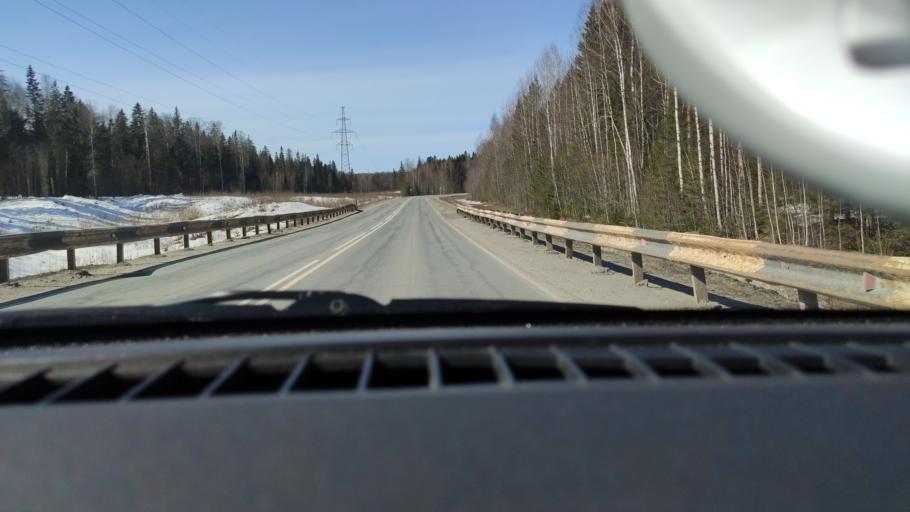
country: RU
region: Perm
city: Perm
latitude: 58.1377
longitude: 56.2801
